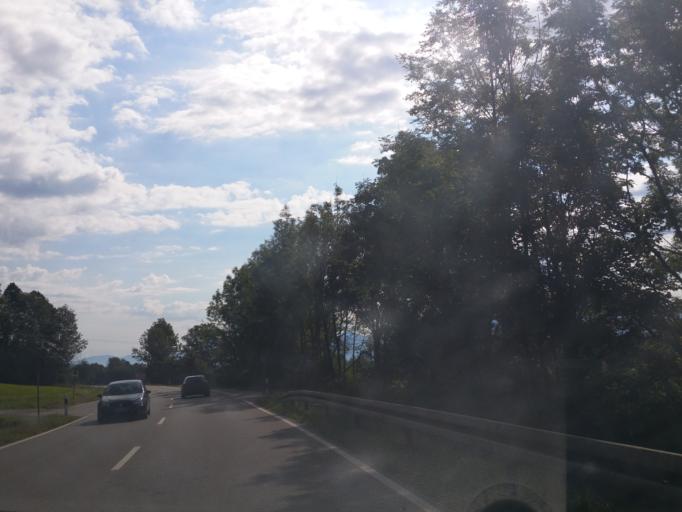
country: DE
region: Bavaria
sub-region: Upper Bavaria
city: Bad Kohlgrub
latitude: 47.6657
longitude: 11.0866
